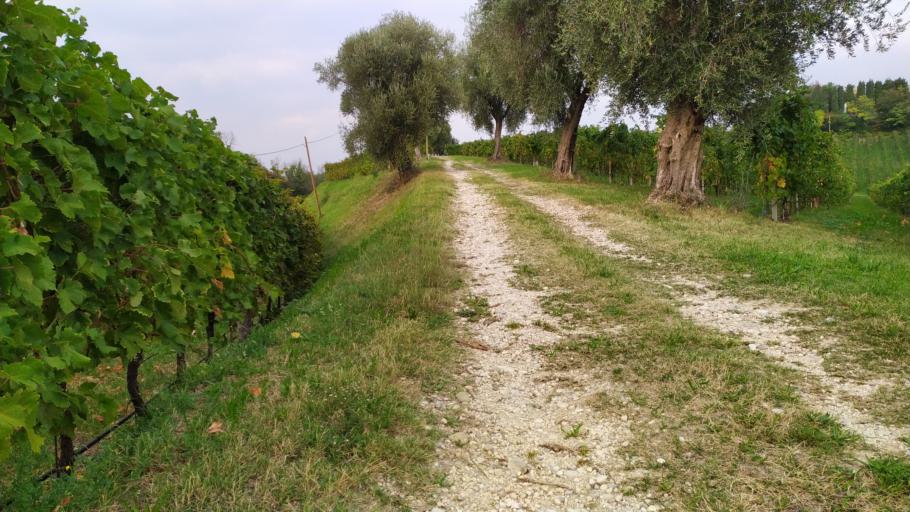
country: IT
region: Veneto
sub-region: Provincia di Treviso
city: Conegliano
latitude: 45.8865
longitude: 12.2778
